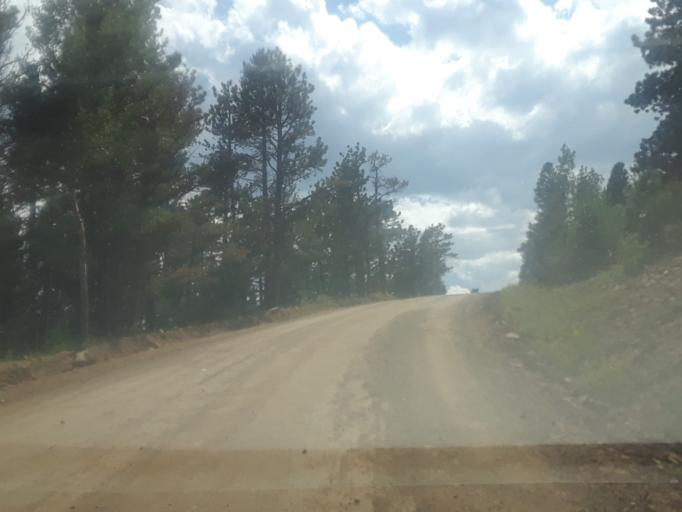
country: US
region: Colorado
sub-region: Boulder County
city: Nederland
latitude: 40.0464
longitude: -105.4926
